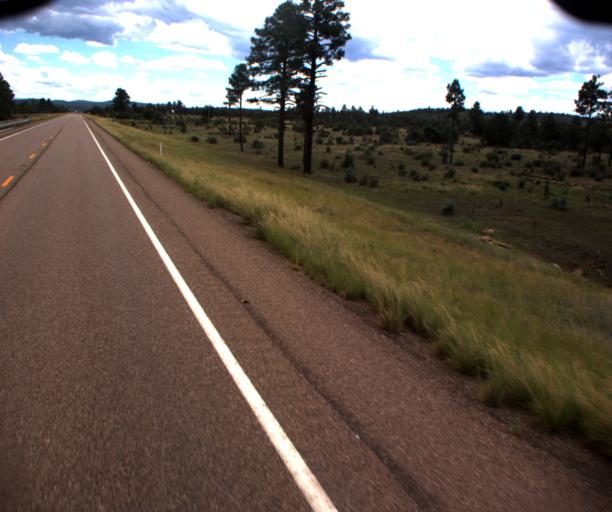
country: US
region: Arizona
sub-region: Navajo County
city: Linden
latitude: 34.3294
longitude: -110.2634
